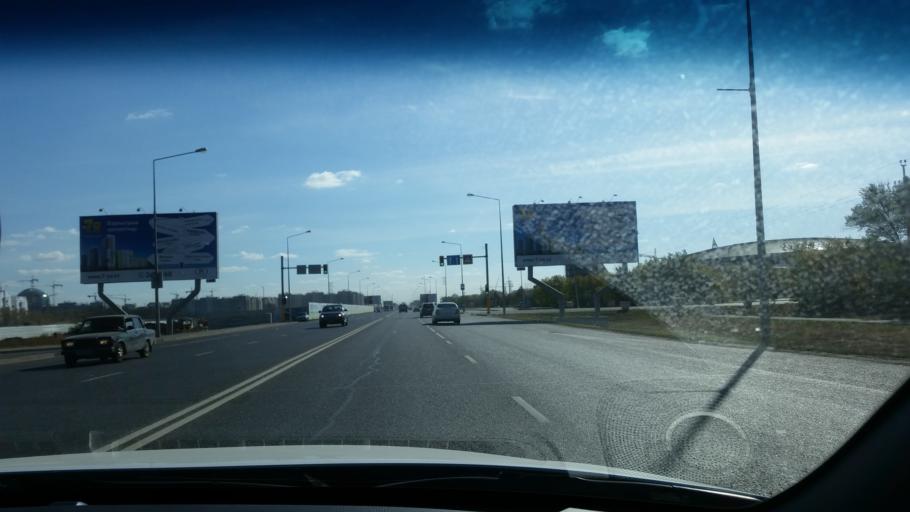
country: KZ
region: Astana Qalasy
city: Astana
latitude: 51.1082
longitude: 71.4094
